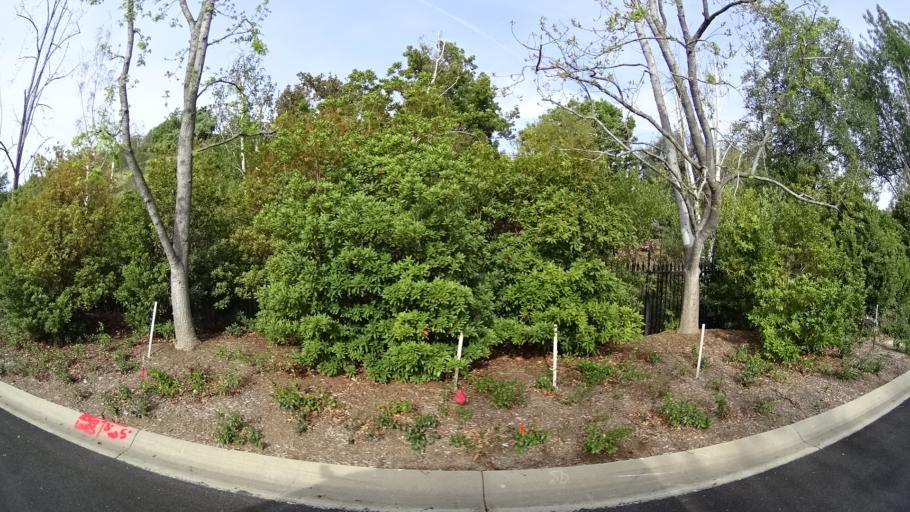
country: US
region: California
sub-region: Ventura County
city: Thousand Oaks
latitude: 34.1996
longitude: -118.8203
